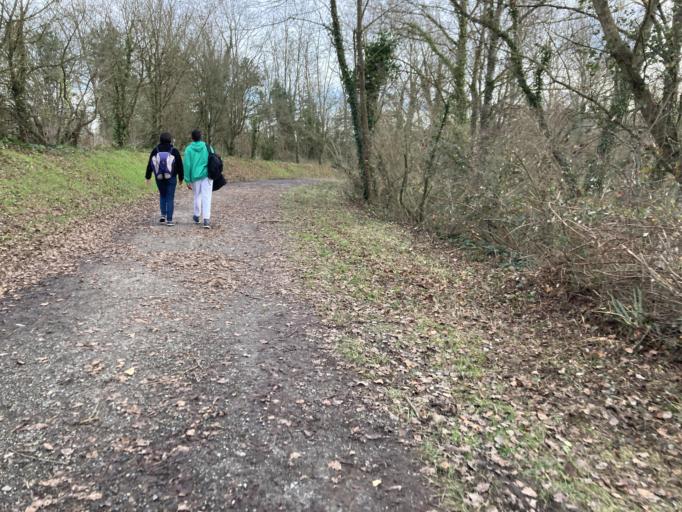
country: FR
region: Aquitaine
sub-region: Departement des Pyrenees-Atlantiques
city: Artiguelouve
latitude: 43.3149
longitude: -0.4434
